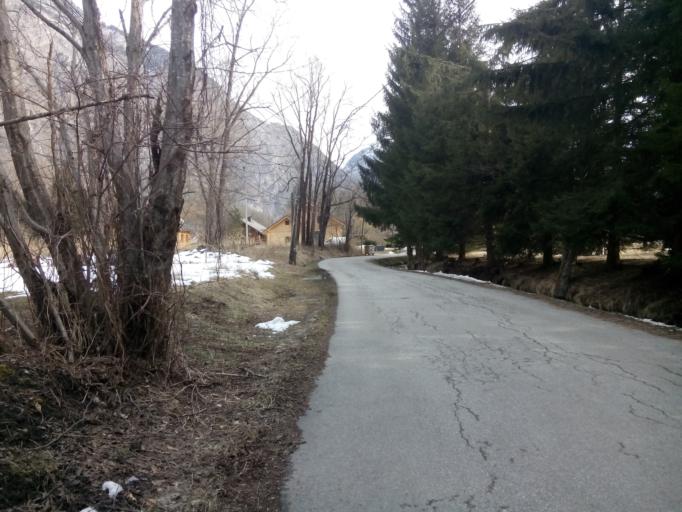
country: FR
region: Rhone-Alpes
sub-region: Departement de l'Isere
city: Huez
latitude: 45.0465
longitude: 6.0465
